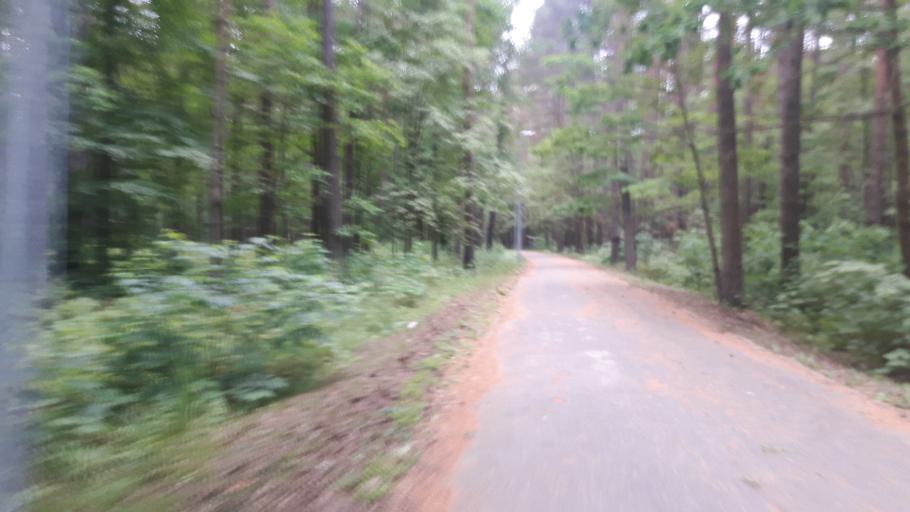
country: LV
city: Tireli
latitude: 56.9568
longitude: 23.6405
